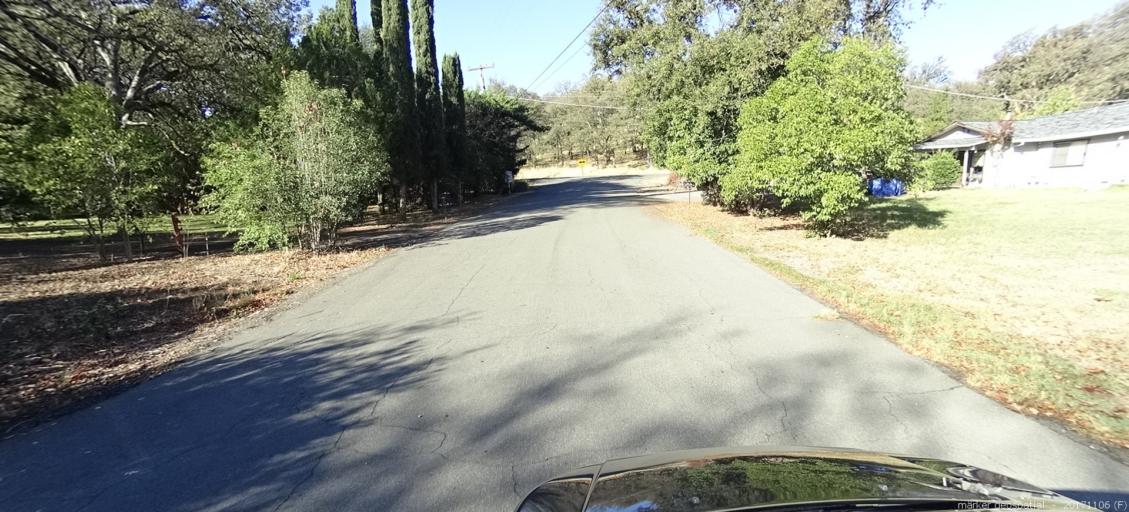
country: US
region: California
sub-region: Shasta County
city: Palo Cedro
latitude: 40.5462
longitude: -122.2449
